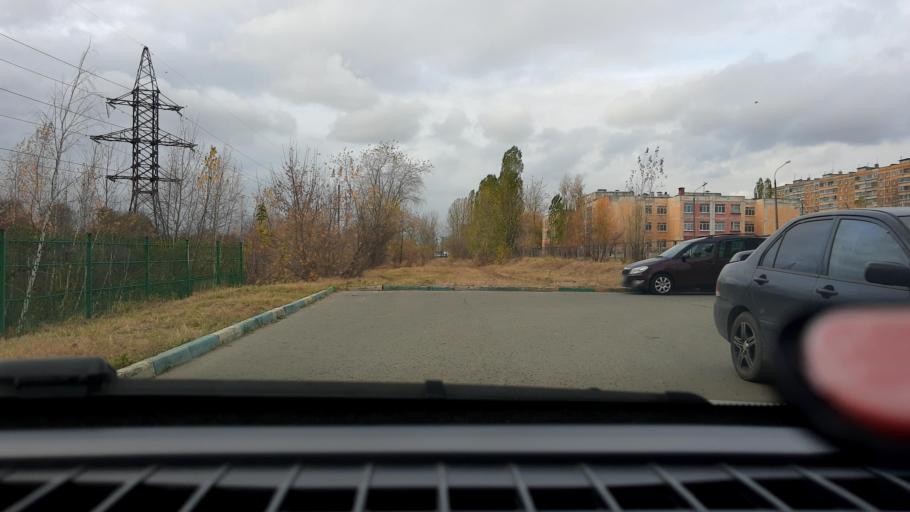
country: RU
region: Nizjnij Novgorod
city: Burevestnik
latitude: 56.2183
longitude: 43.8562
